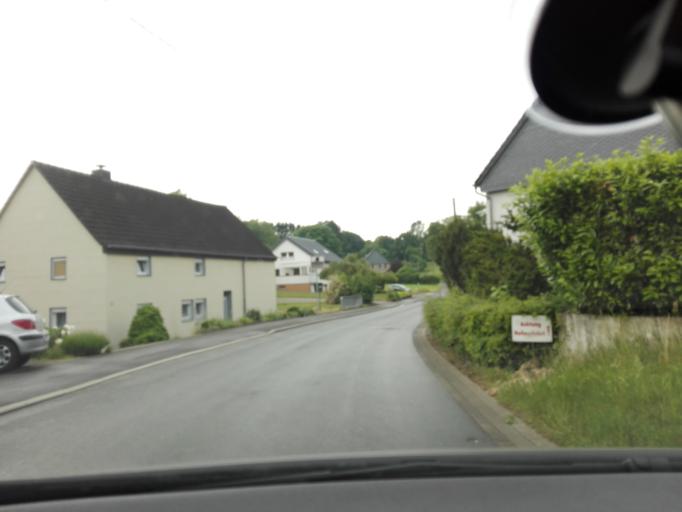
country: DE
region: North Rhine-Westphalia
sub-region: Regierungsbezirk Arnsberg
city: Unna
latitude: 51.5214
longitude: 7.7224
